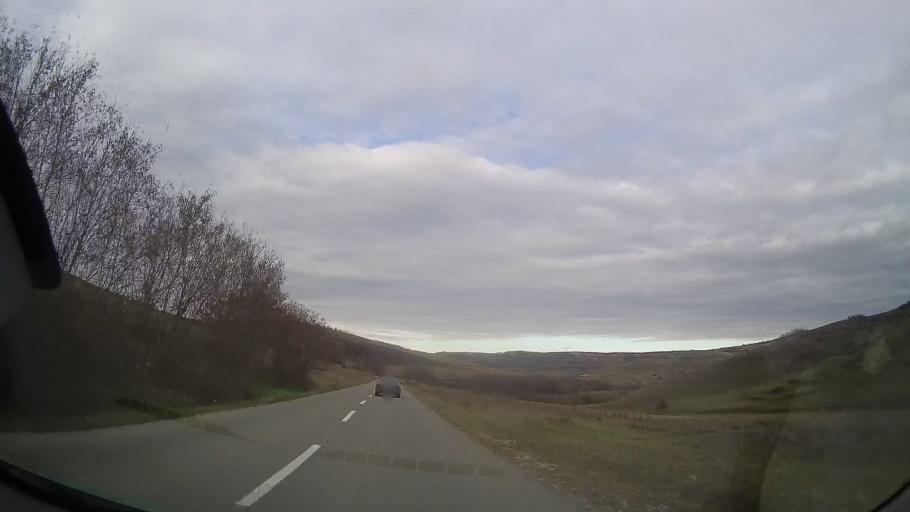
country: RO
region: Bistrita-Nasaud
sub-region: Comuna Milas
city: Milas
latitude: 46.8288
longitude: 24.4486
